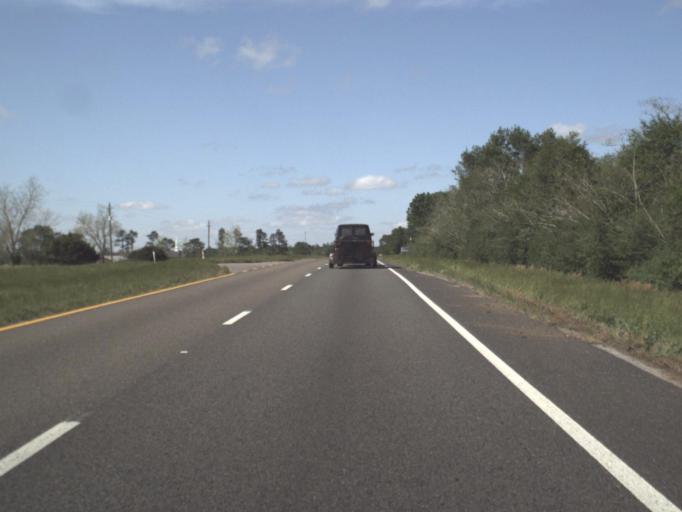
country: US
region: Florida
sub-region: Escambia County
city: Molino
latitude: 30.7200
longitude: -87.3495
